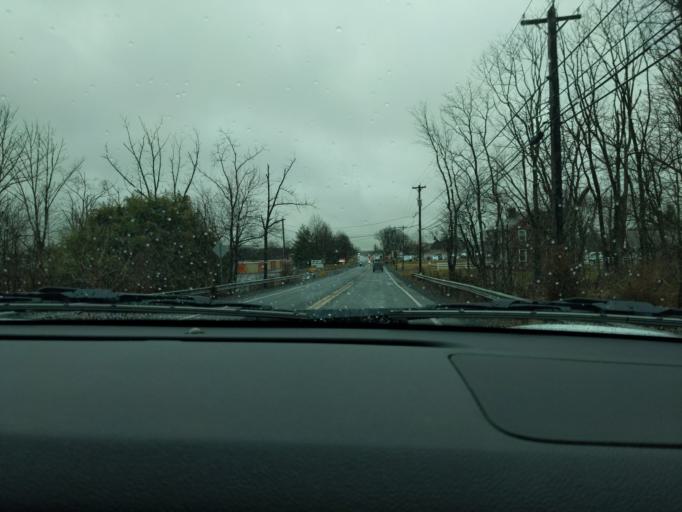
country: US
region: Pennsylvania
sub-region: Bucks County
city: Dublin
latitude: 40.3784
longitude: -75.2136
